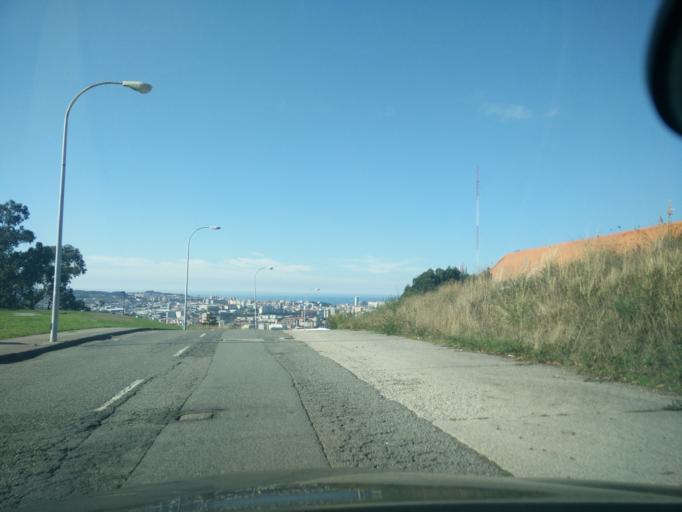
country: ES
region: Galicia
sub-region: Provincia da Coruna
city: Culleredo
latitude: 43.3261
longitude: -8.4067
